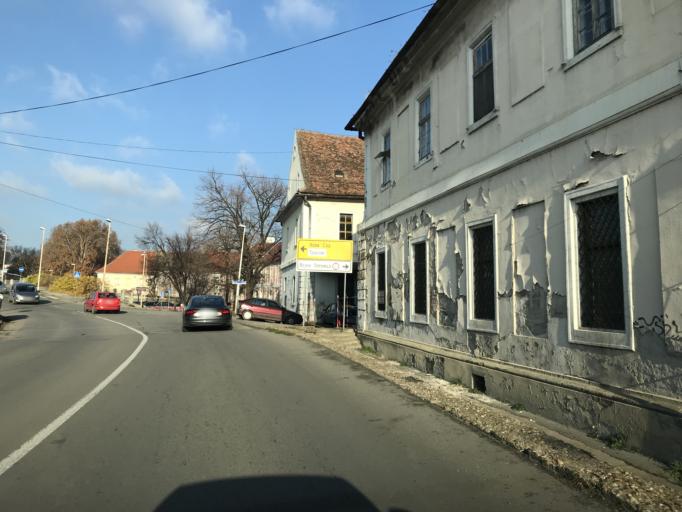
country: RS
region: Autonomna Pokrajina Vojvodina
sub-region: Juznobacki Okrug
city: Petrovaradin
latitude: 45.2538
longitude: 19.8602
